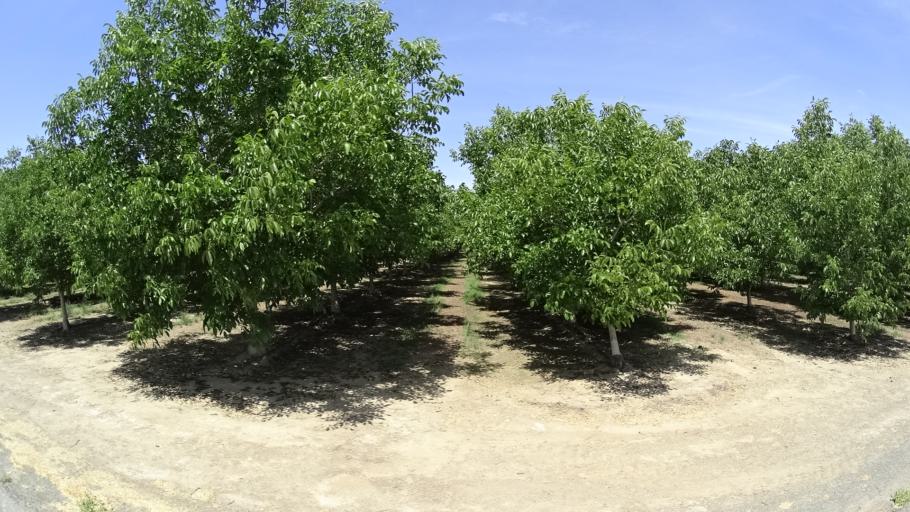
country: US
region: California
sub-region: Kings County
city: Armona
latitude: 36.2838
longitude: -119.6855
